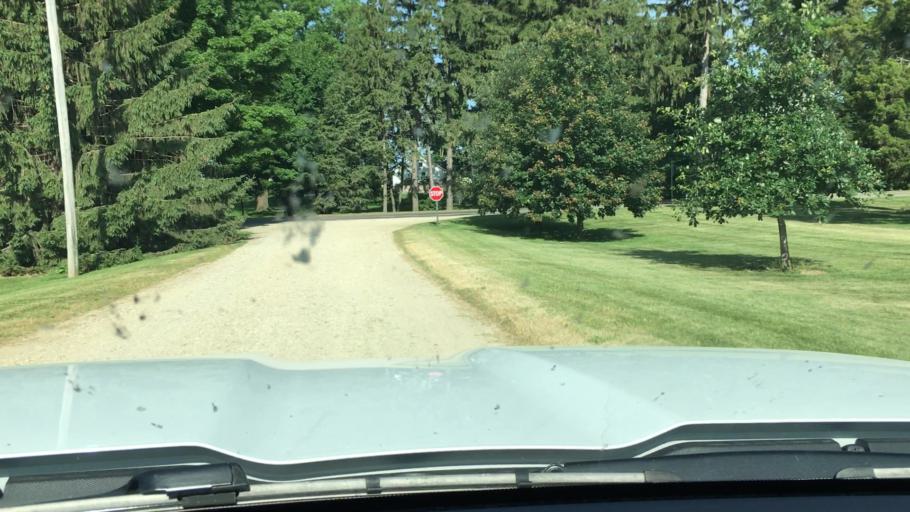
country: US
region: Michigan
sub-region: Kalamazoo County
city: South Gull Lake
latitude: 42.4268
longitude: -85.4539
